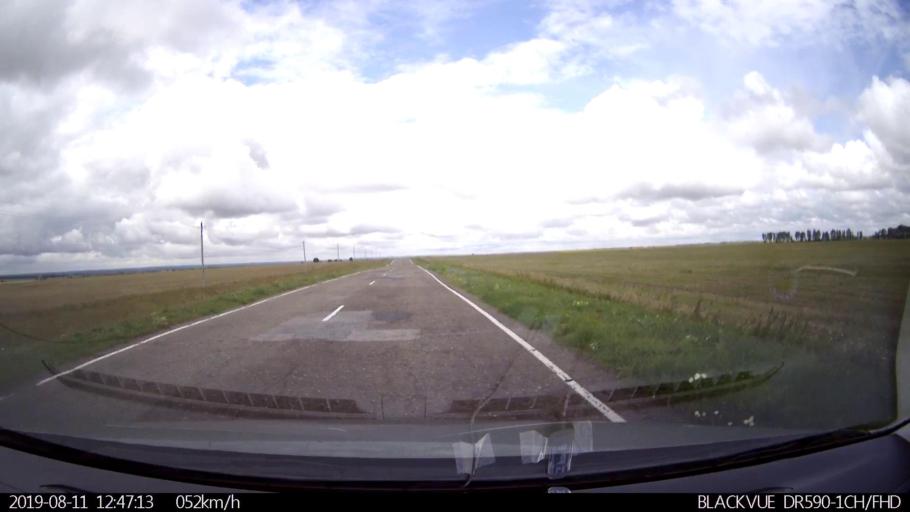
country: RU
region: Ulyanovsk
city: Ignatovka
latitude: 53.8685
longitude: 47.7107
